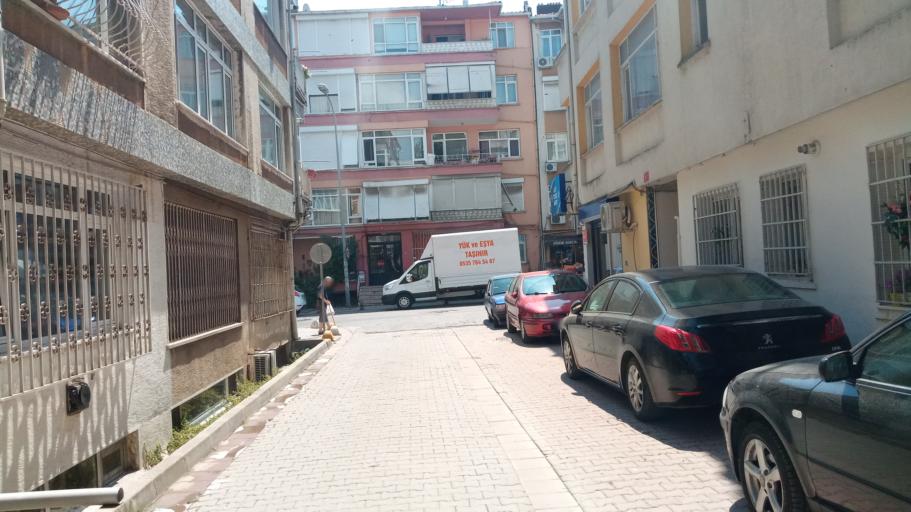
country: TR
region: Istanbul
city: UEskuedar
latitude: 40.9876
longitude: 29.0313
